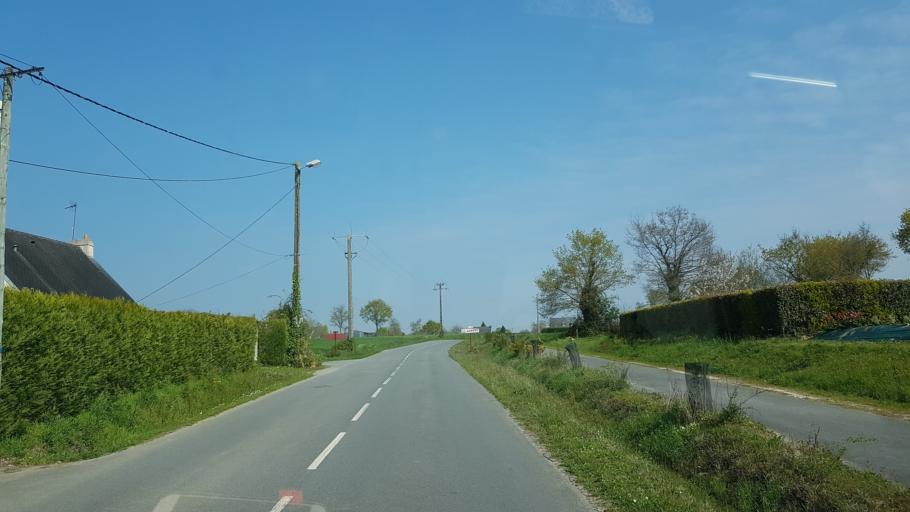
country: FR
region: Brittany
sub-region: Departement du Morbihan
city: Noyal-Muzillac
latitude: 47.5859
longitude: -2.4061
